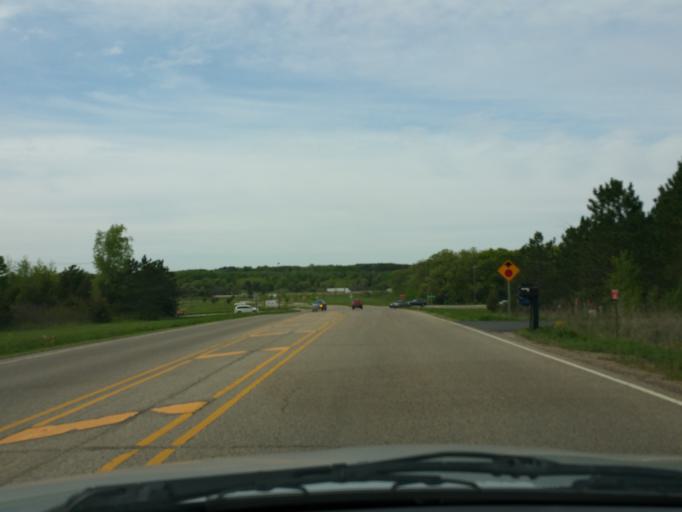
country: US
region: Wisconsin
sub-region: Saint Croix County
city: Hudson
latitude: 44.9576
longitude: -92.6905
